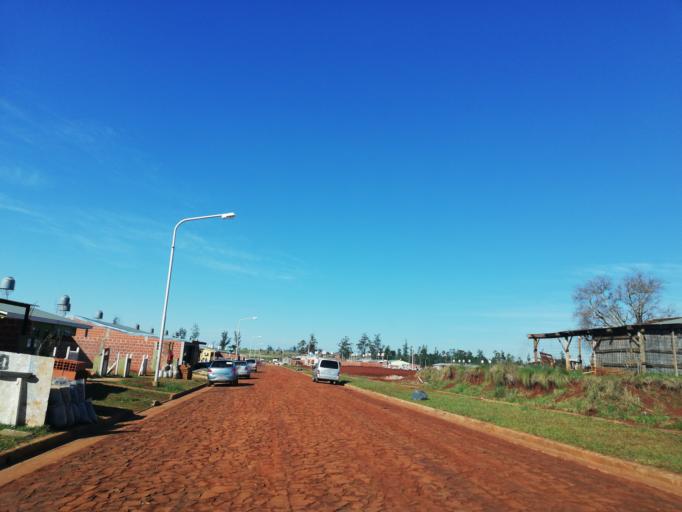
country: AR
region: Misiones
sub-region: Departamento de Capital
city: Posadas
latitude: -27.4158
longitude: -55.9918
